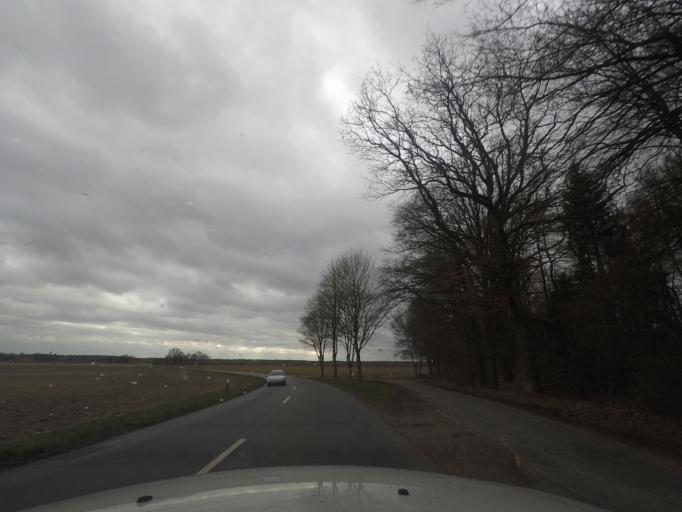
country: DE
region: Lower Saxony
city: Emmendorf
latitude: 53.0161
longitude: 10.5989
